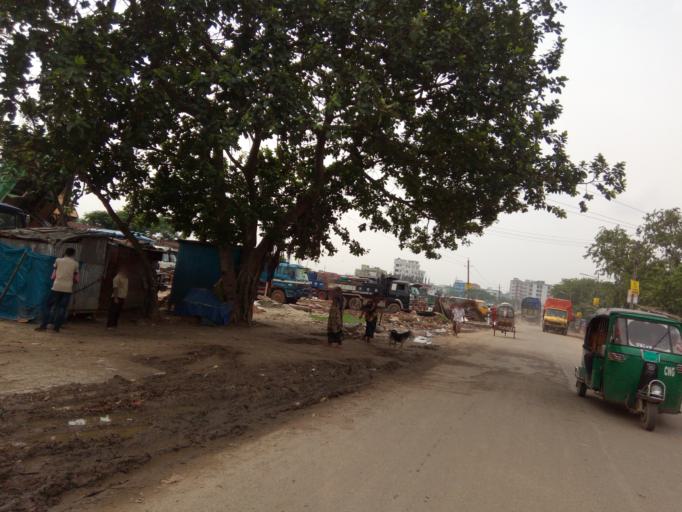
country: BD
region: Dhaka
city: Azimpur
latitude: 23.7539
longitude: 90.3572
